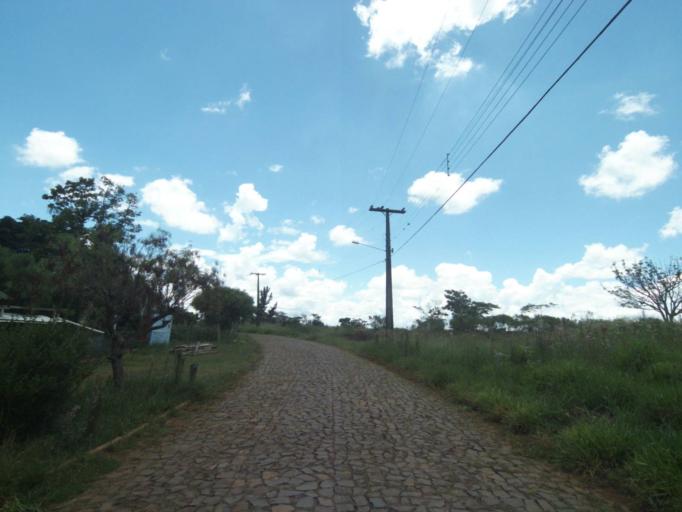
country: BR
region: Parana
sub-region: Pinhao
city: Pinhao
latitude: -25.7898
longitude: -52.0823
